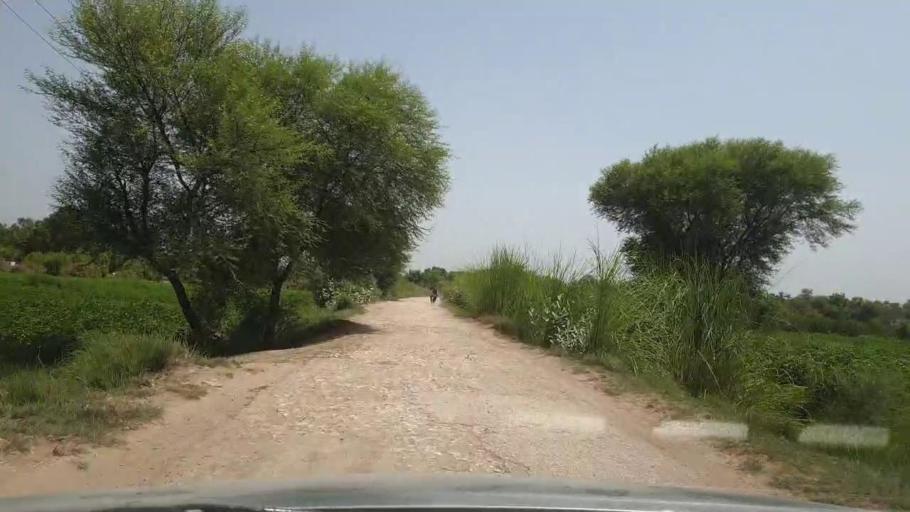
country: PK
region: Sindh
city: Pano Aqil
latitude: 27.8184
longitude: 69.2299
